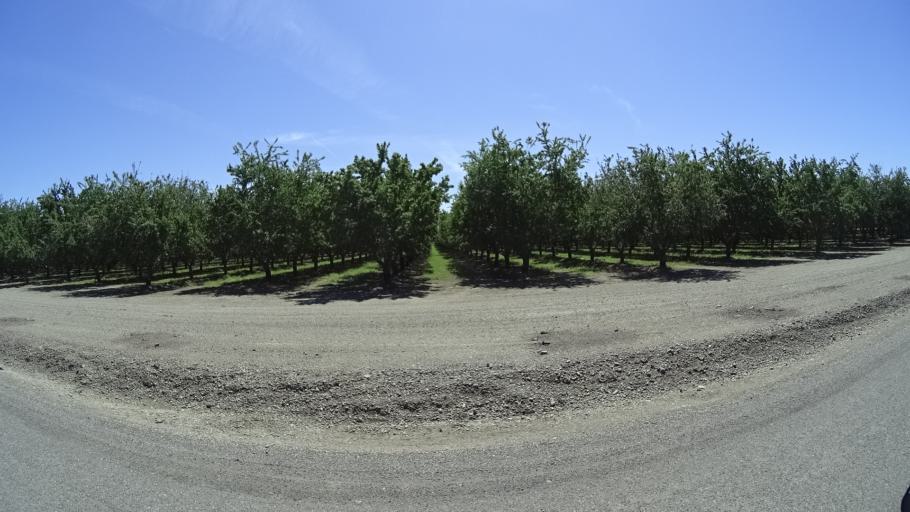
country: US
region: California
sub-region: Glenn County
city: Orland
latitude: 39.7323
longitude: -122.1392
